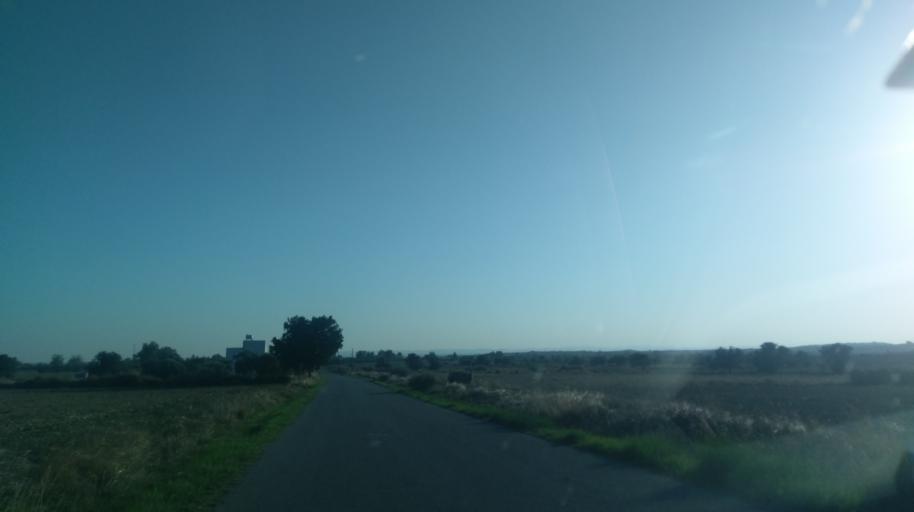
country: CY
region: Ammochostos
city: Lefkonoiko
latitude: 35.2757
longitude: 33.6578
